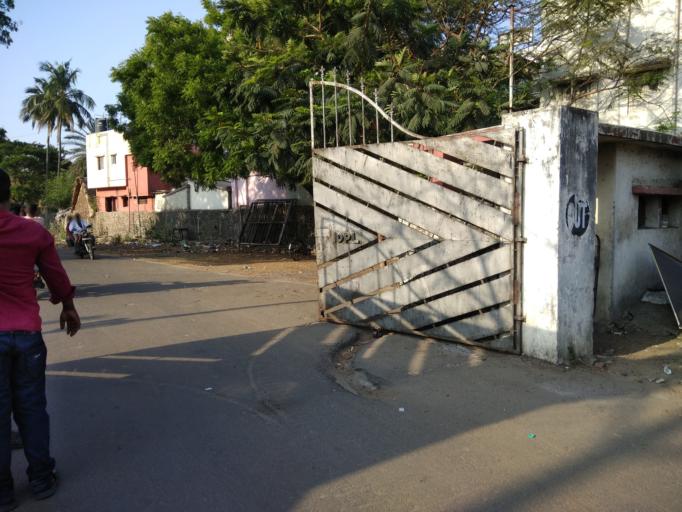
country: IN
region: Tamil Nadu
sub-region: Kancheepuram
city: Saint Thomas Mount
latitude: 13.0166
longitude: 80.1900
